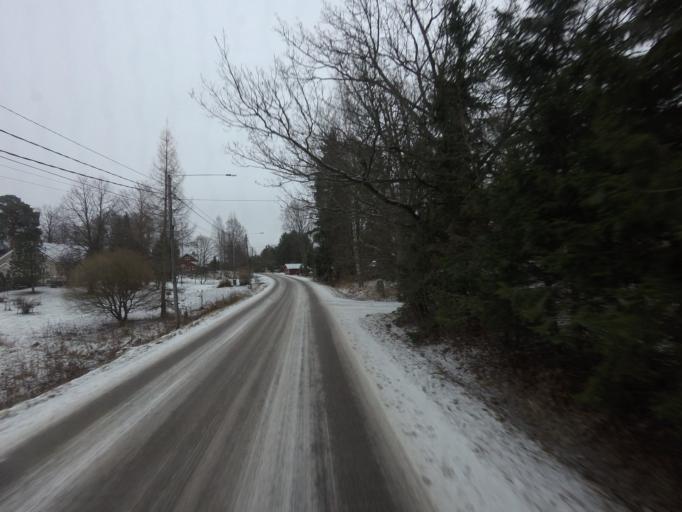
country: FI
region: Uusimaa
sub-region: Helsinki
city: Espoo
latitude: 60.1987
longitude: 24.5595
